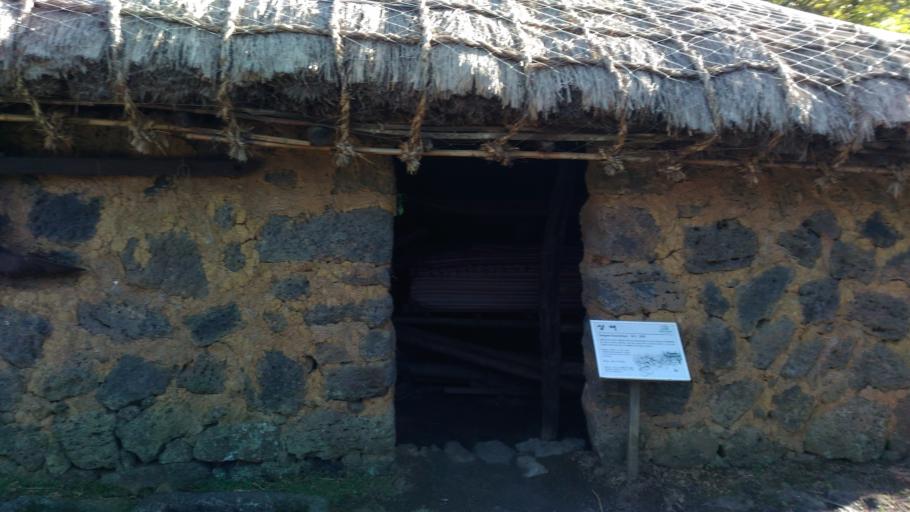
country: KR
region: Jeju-do
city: Seogwipo
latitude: 33.3232
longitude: 126.8404
